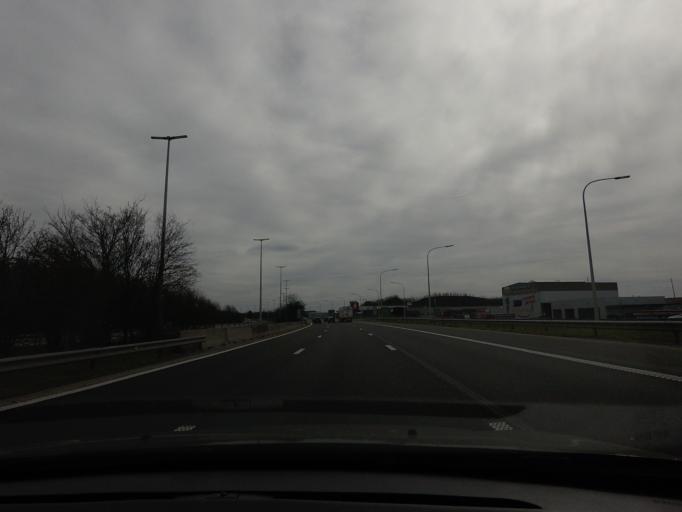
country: BE
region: Wallonia
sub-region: Province de Liege
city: Ans
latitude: 50.6580
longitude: 5.5011
